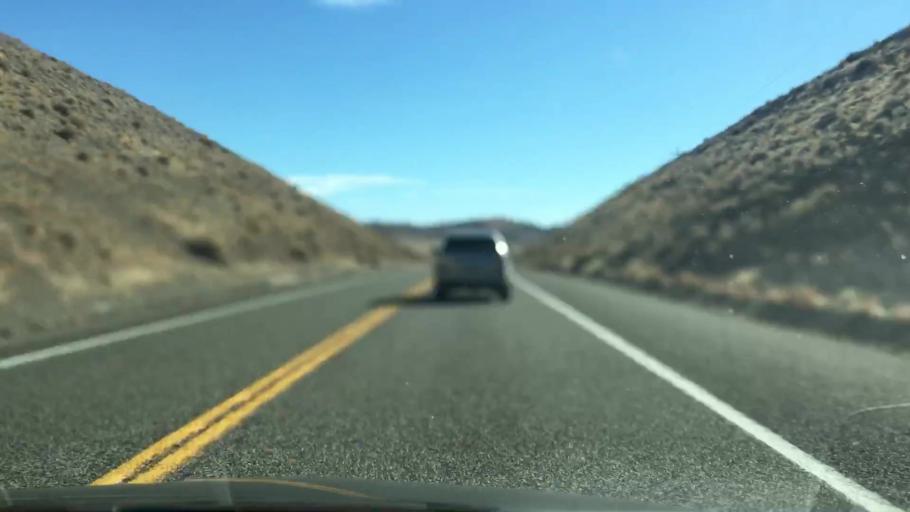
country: US
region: Nevada
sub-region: Lyon County
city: Silver Springs
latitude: 39.2139
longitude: -119.2196
